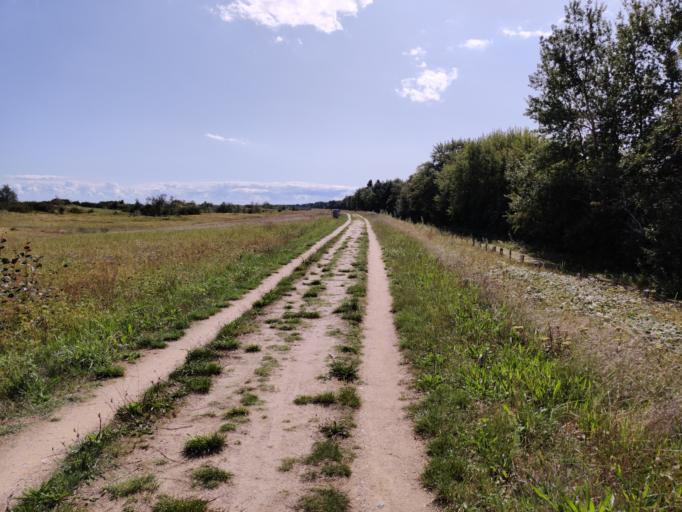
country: DK
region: Zealand
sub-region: Guldborgsund Kommune
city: Nykobing Falster
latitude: 54.6745
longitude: 11.9618
